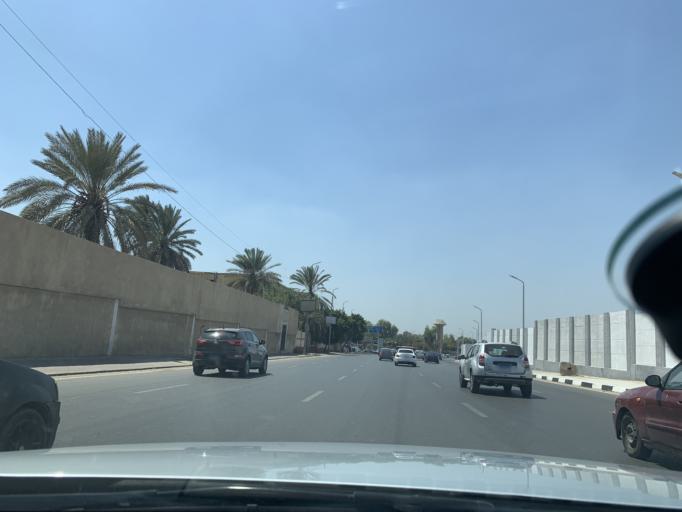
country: EG
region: Muhafazat al Qahirah
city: Cairo
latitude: 30.0888
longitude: 31.3501
